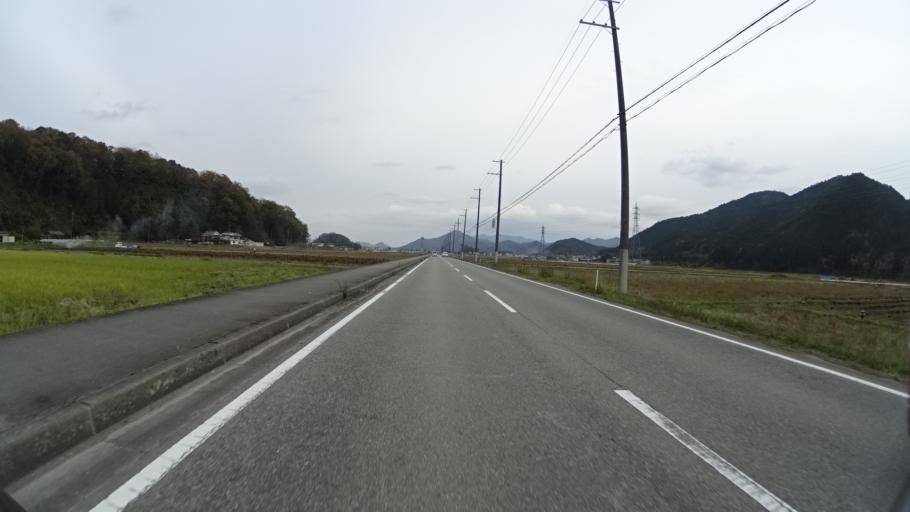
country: JP
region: Hyogo
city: Sasayama
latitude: 35.0636
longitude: 135.2043
